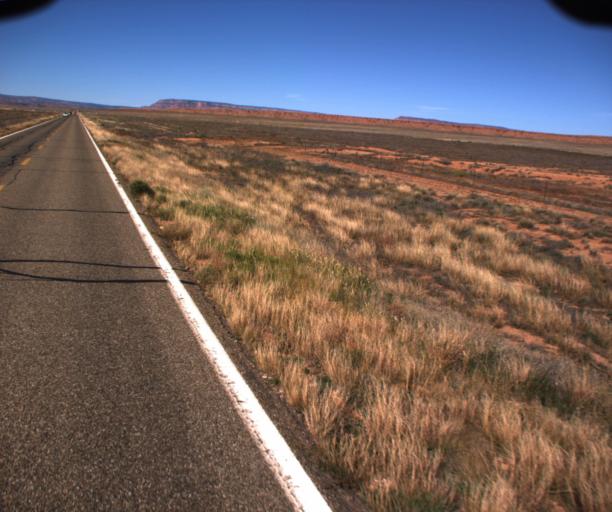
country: US
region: Arizona
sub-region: Coconino County
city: Fredonia
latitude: 36.9236
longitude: -112.4540
